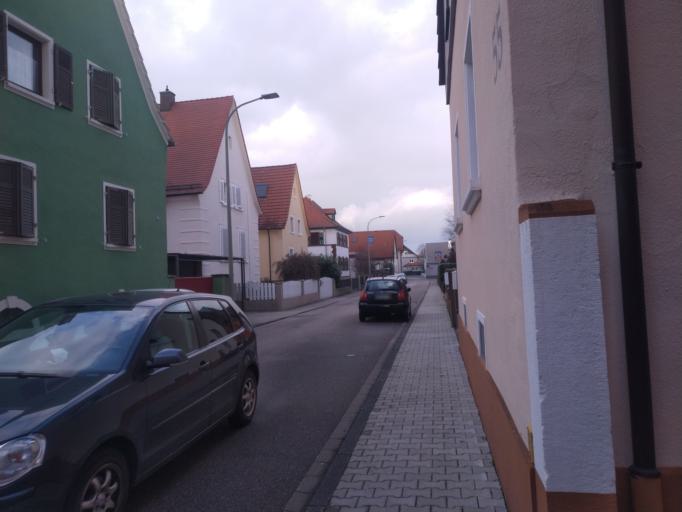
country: DE
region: Rheinland-Pfalz
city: Worth am Rhein
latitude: 49.0327
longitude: 8.2864
